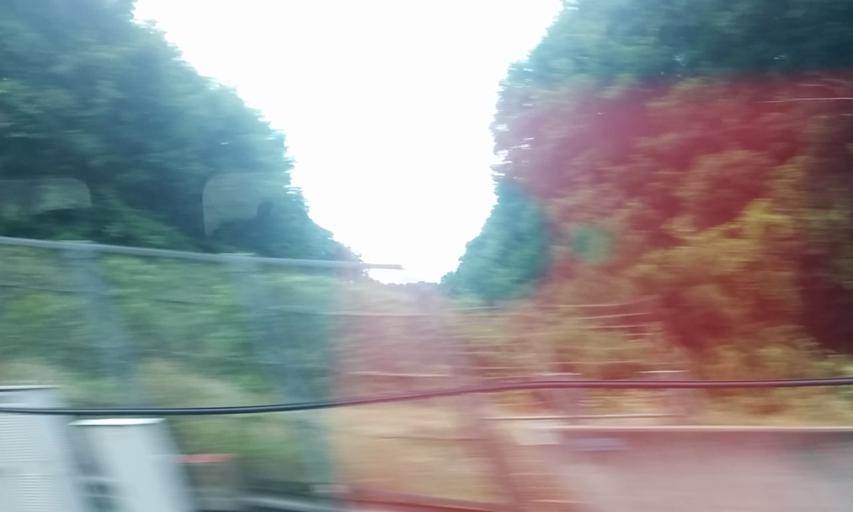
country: JP
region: Fukushima
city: Sukagawa
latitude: 37.3174
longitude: 140.3528
